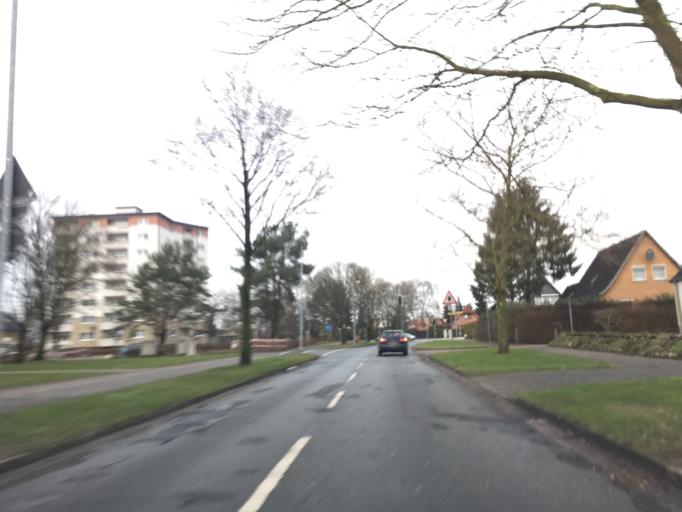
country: DE
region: Schleswig-Holstein
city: Wahlstedt
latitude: 53.9542
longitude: 10.2017
